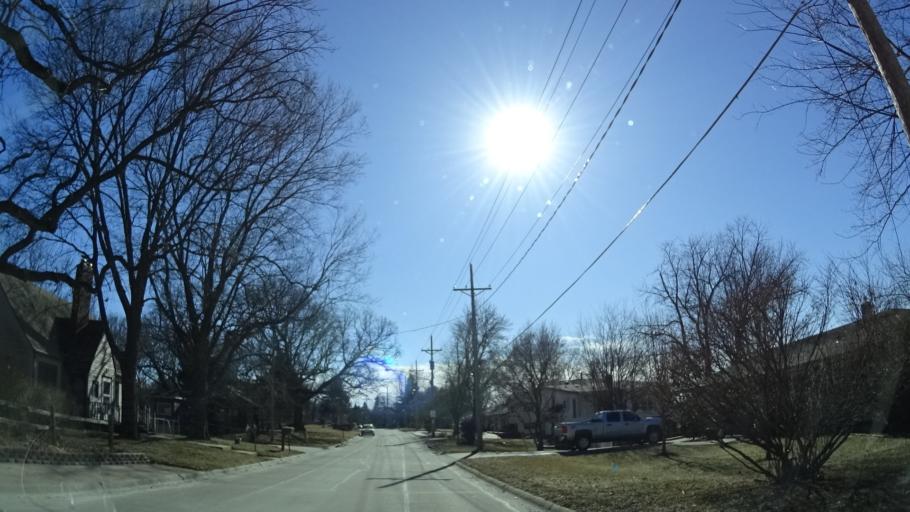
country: US
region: Nebraska
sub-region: Sarpy County
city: Bellevue
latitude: 41.1508
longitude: -95.9004
